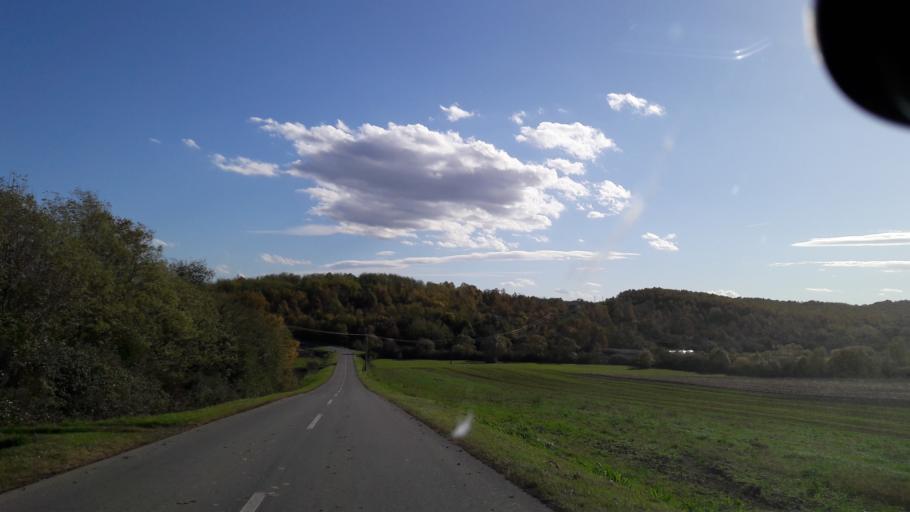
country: HR
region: Osjecko-Baranjska
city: Vukojevci
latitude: 45.3920
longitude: 18.2427
